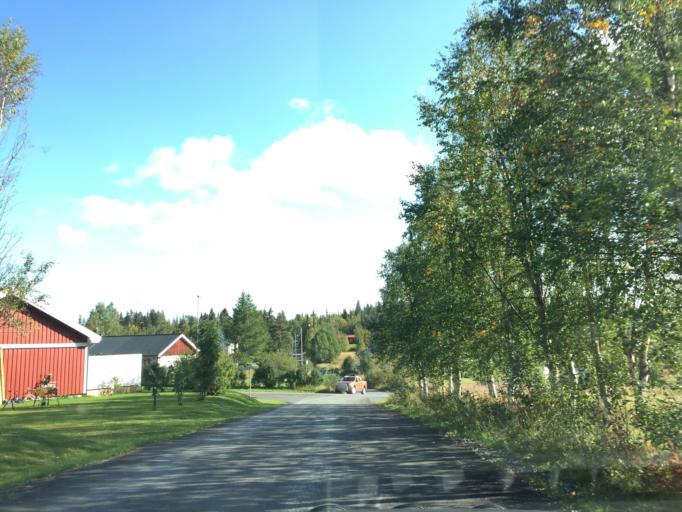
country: SE
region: Norrbotten
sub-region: Gallivare Kommun
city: Malmberget
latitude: 67.6471
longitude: 21.0627
